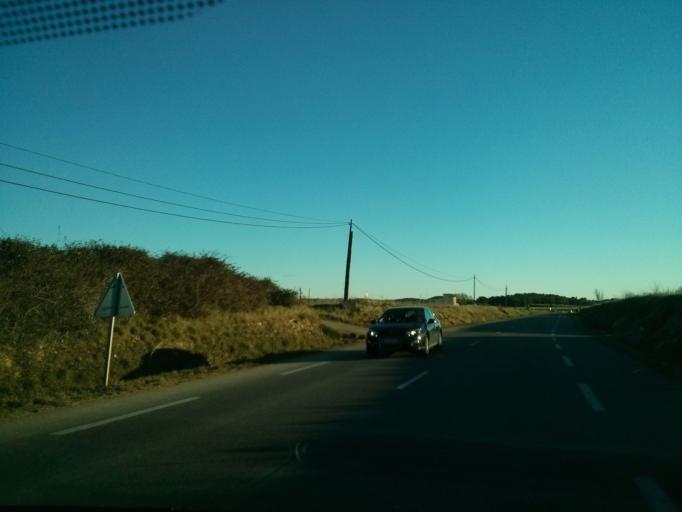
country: FR
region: Languedoc-Roussillon
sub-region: Departement du Gard
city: Calvisson
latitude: 43.7715
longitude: 4.2001
